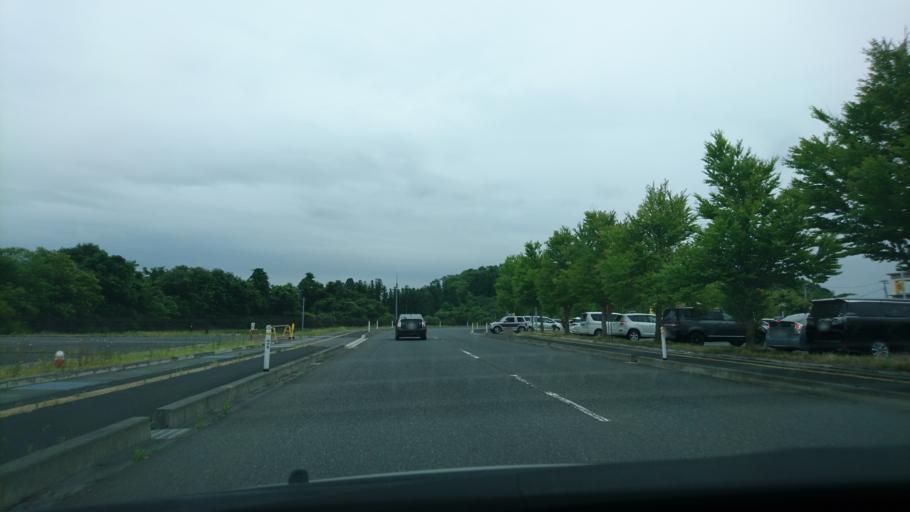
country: JP
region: Iwate
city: Ichinoseki
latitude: 38.9347
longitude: 141.1706
